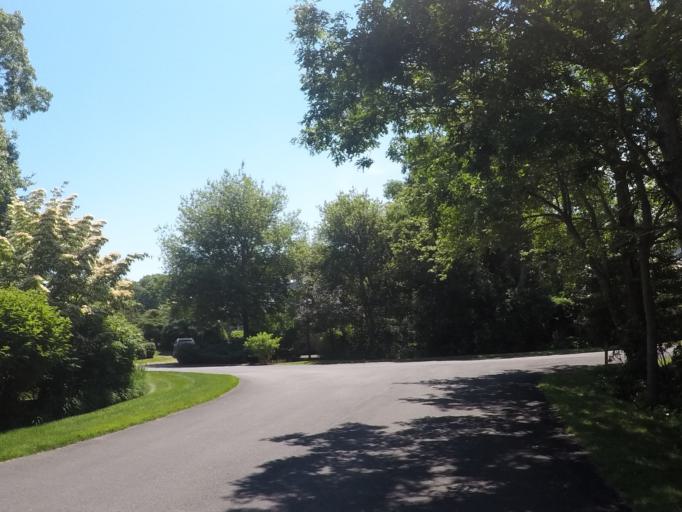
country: US
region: Massachusetts
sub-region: Bristol County
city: Bliss Corner
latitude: 41.5445
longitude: -70.9469
